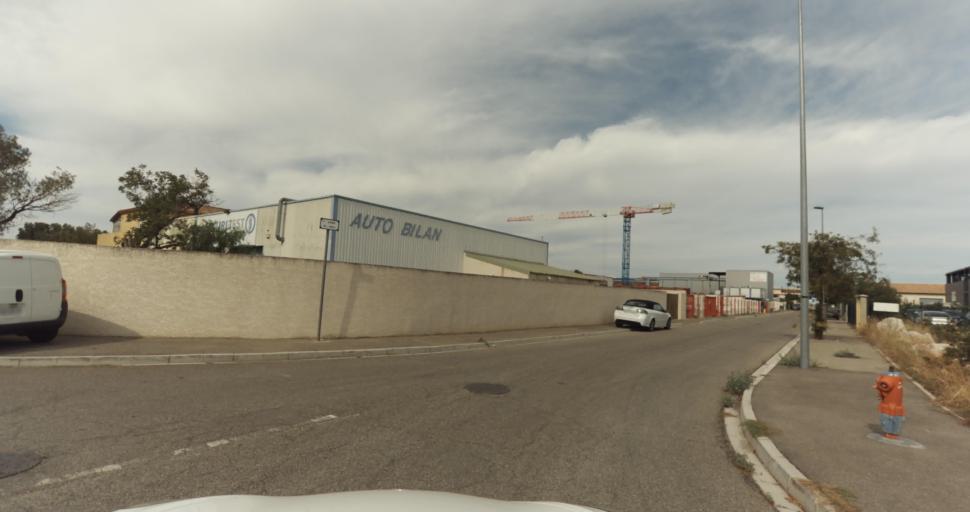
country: FR
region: Provence-Alpes-Cote d'Azur
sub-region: Departement des Bouches-du-Rhone
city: Miramas
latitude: 43.5961
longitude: 4.9947
